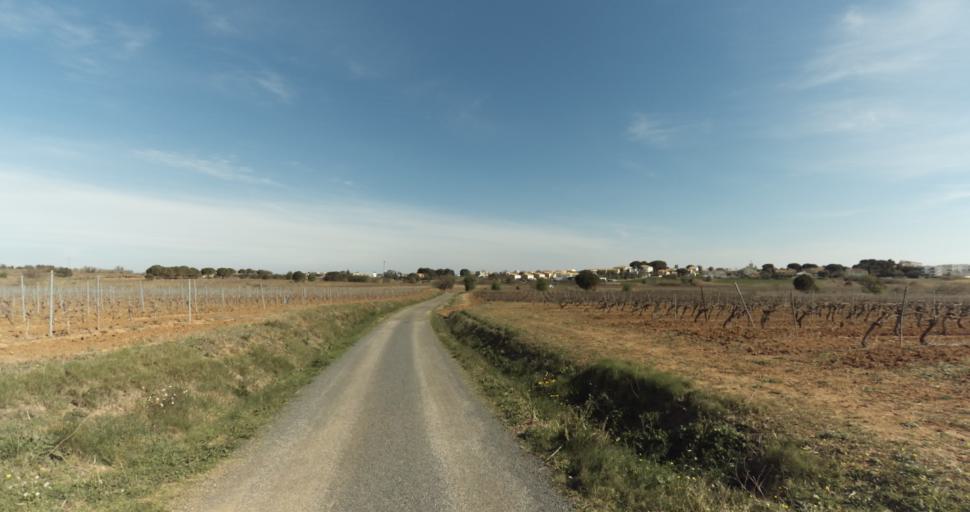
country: FR
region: Languedoc-Roussillon
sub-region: Departement de l'Herault
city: Marseillan
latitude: 43.3484
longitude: 3.5186
